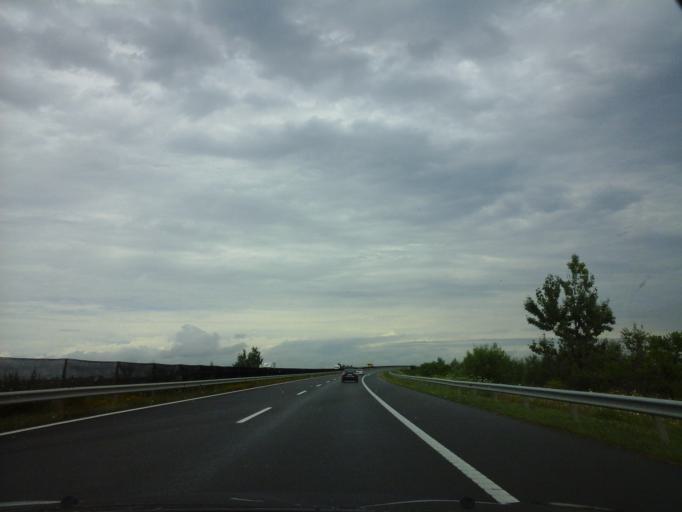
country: HU
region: Hajdu-Bihar
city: Polgar
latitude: 47.8158
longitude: 21.1551
